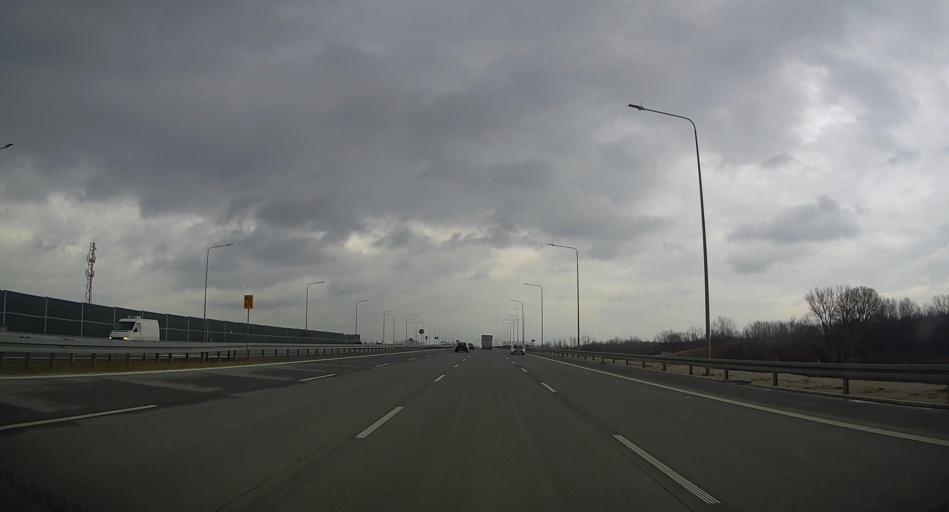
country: PL
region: Masovian Voivodeship
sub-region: Warszawa
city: Wilanow
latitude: 52.1594
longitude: 21.1330
